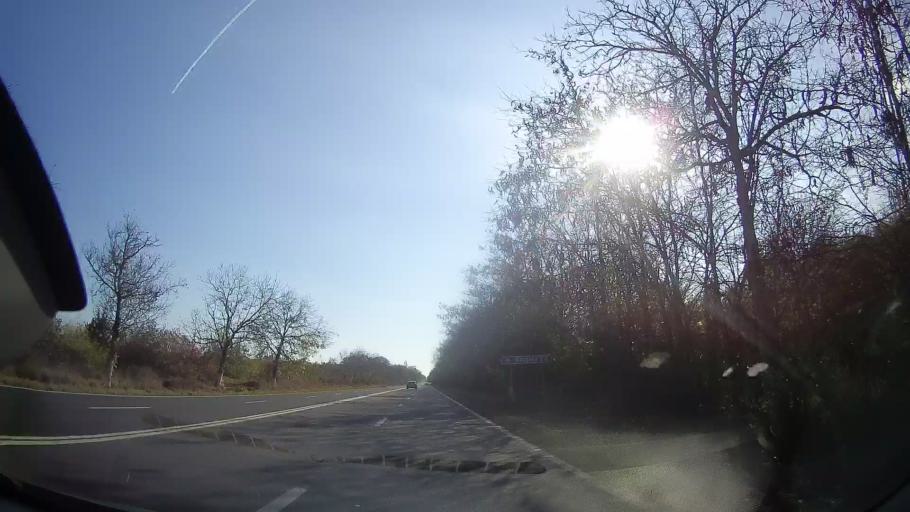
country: RO
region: Constanta
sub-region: Comuna Douazeci si Trei August
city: Dulcesti
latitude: 43.8805
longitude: 28.5735
